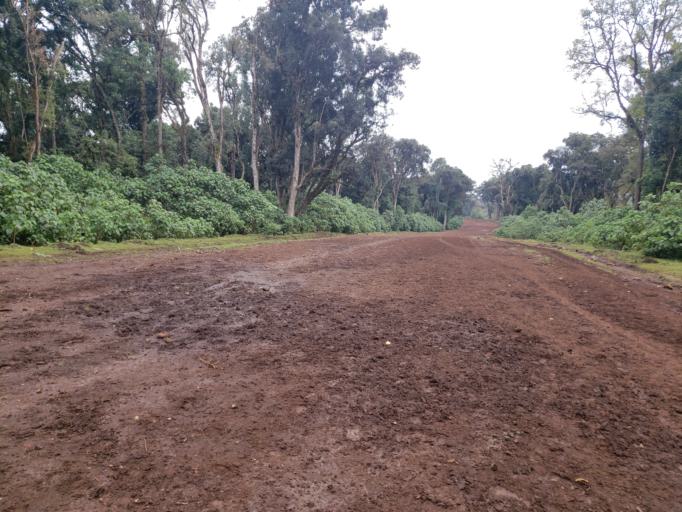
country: ET
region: Oromiya
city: Dodola
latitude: 6.6066
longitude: 39.4166
